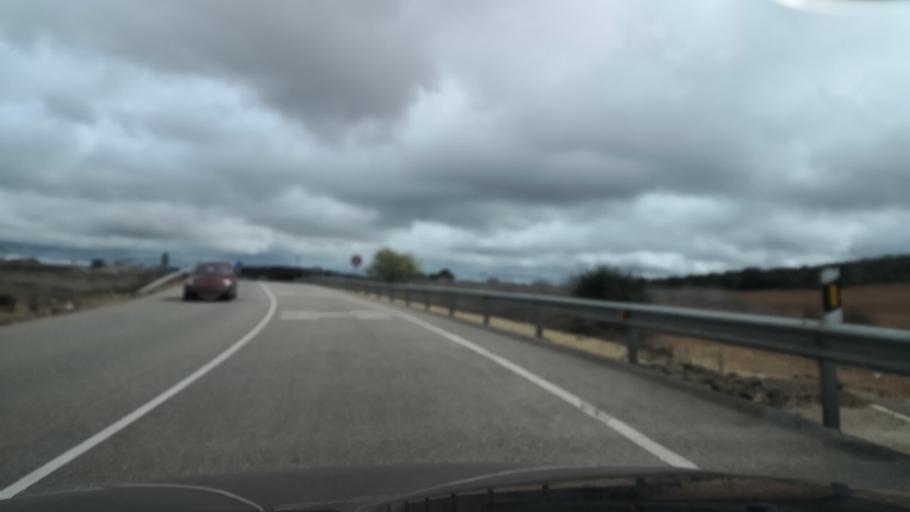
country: ES
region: Castille and Leon
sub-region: Provincia de Zamora
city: Montamarta
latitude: 41.6901
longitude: -5.8093
